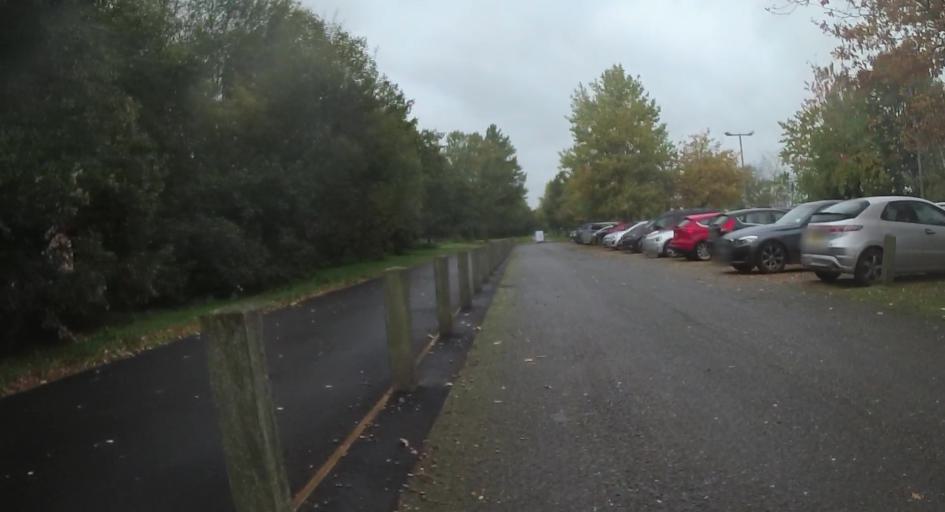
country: GB
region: England
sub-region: Surrey
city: Byfleet
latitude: 51.3530
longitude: -0.4661
